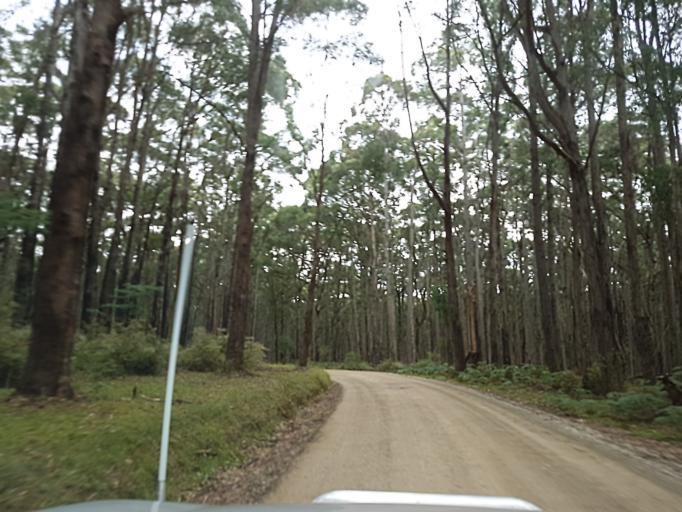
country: AU
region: Victoria
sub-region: Yarra Ranges
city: Mount Dandenong
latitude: -37.8372
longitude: 145.3973
